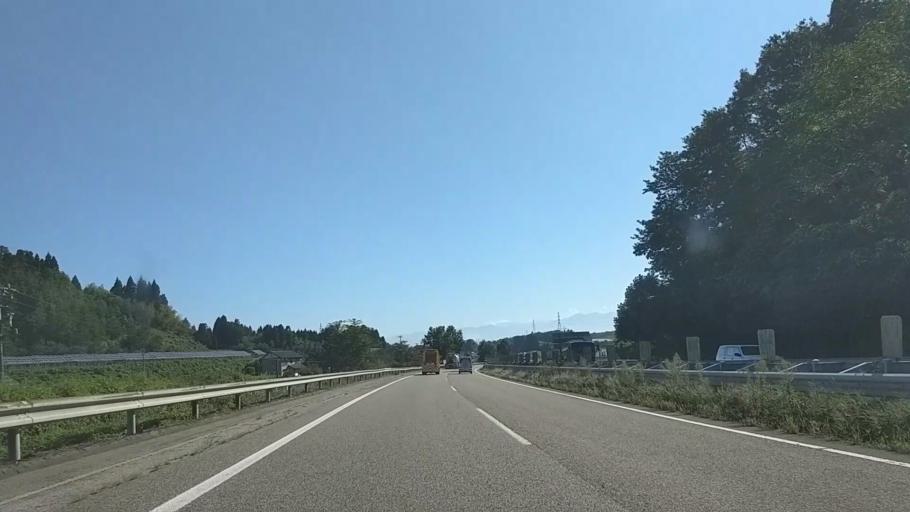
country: JP
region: Toyama
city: Takaoka
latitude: 36.6898
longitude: 137.0648
